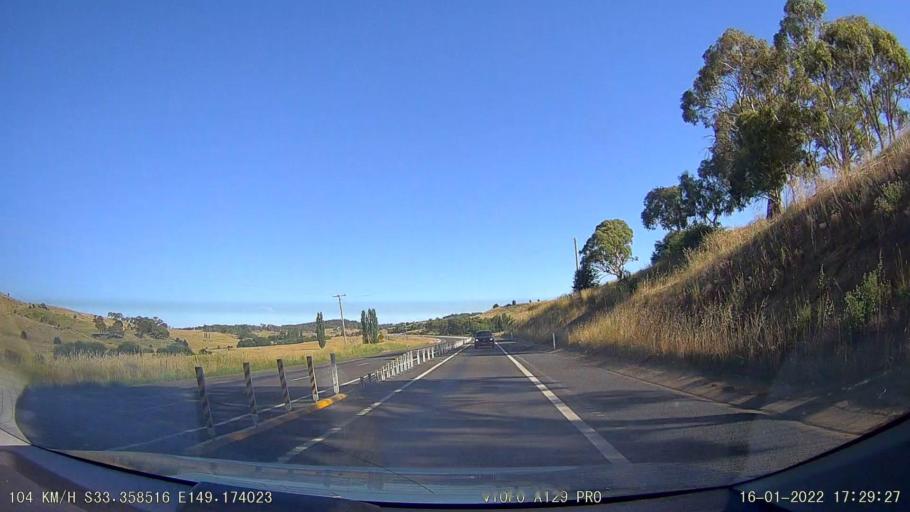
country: AU
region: New South Wales
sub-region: Blayney
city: Millthorpe
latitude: -33.3583
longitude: 149.1736
